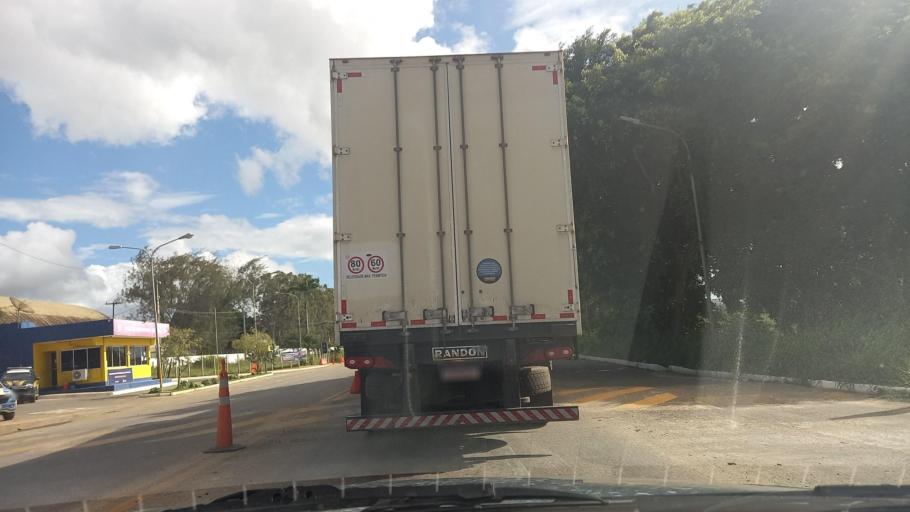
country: BR
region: Pernambuco
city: Garanhuns
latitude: -8.8693
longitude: -36.4626
